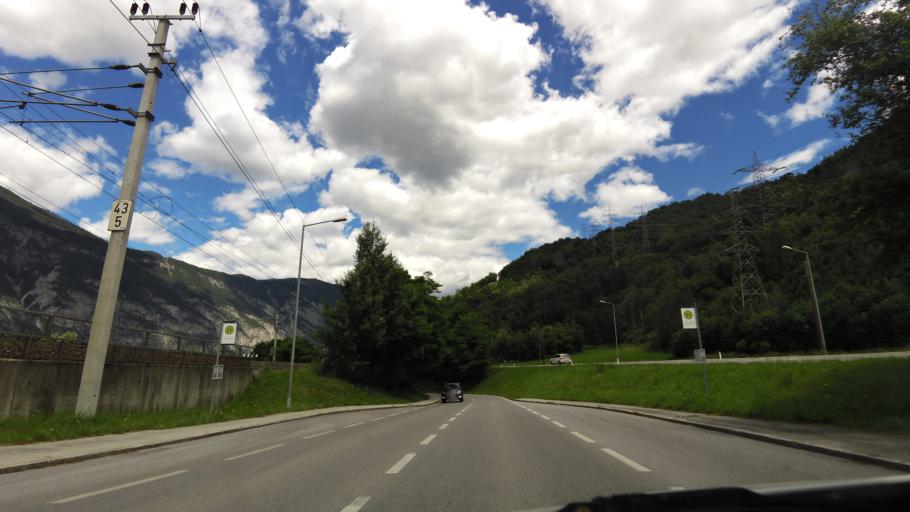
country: AT
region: Tyrol
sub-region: Politischer Bezirk Imst
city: Haiming
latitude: 47.2444
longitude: 10.8816
